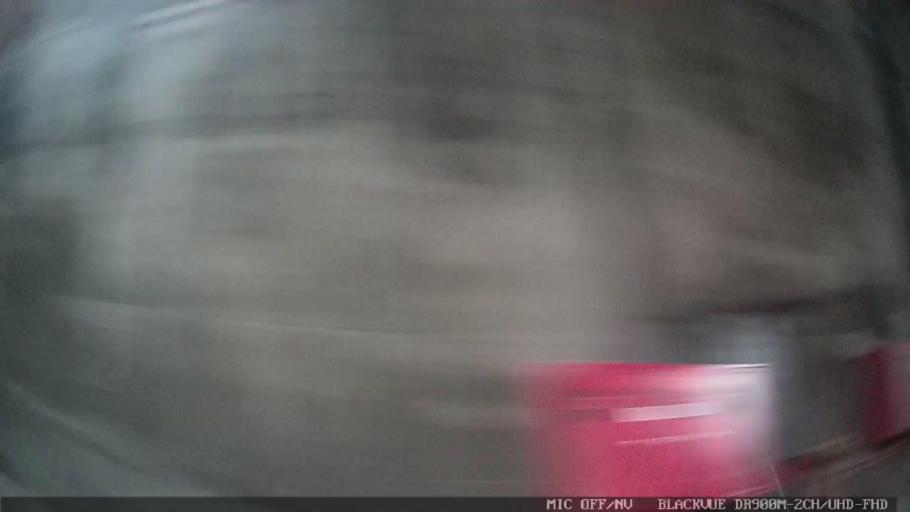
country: BR
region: Sao Paulo
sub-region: Cubatao
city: Cubatao
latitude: -23.9119
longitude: -46.5271
